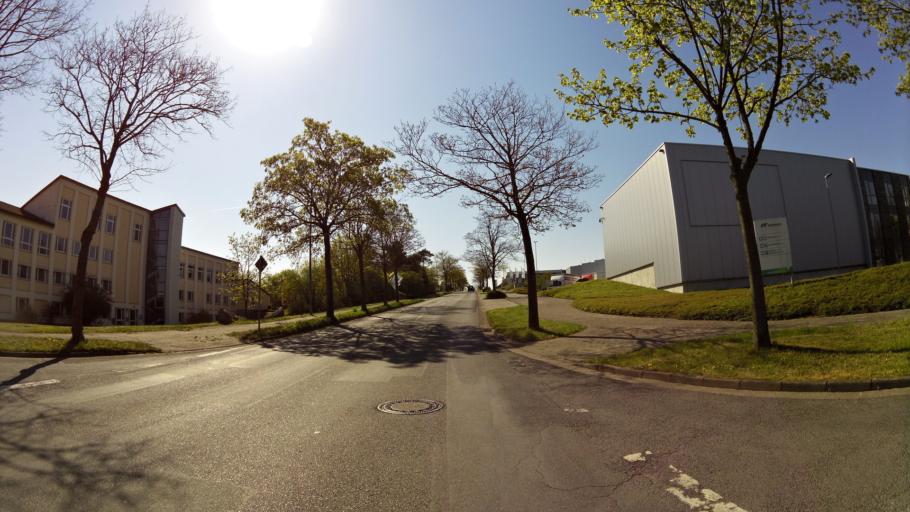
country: DE
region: Lower Saxony
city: Syke
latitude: 52.9185
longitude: 8.8007
